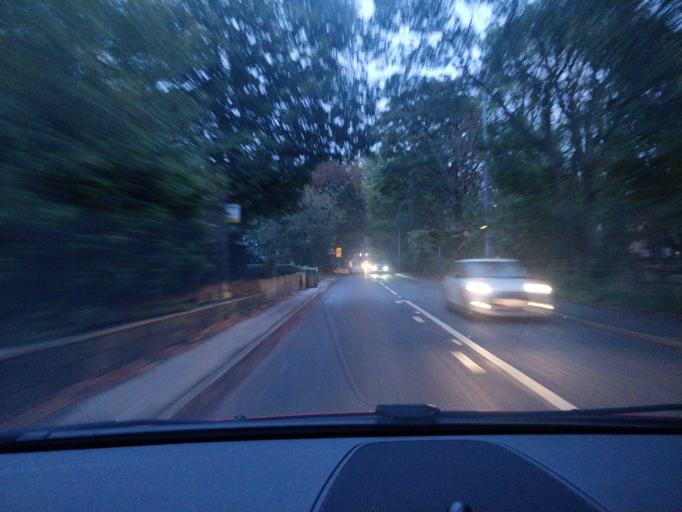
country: GB
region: England
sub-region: Lancashire
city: Ormskirk
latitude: 53.5982
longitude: -2.9253
